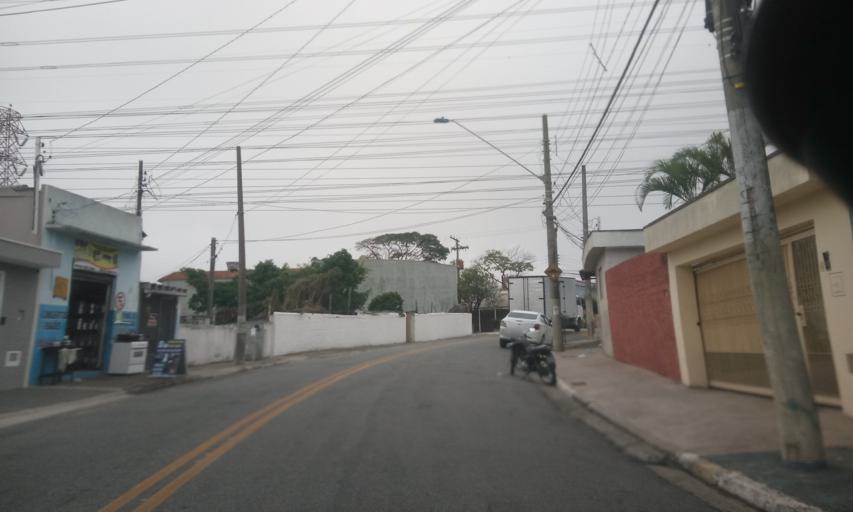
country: BR
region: Sao Paulo
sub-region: Sao Caetano Do Sul
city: Sao Caetano do Sul
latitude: -23.6476
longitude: -46.5694
